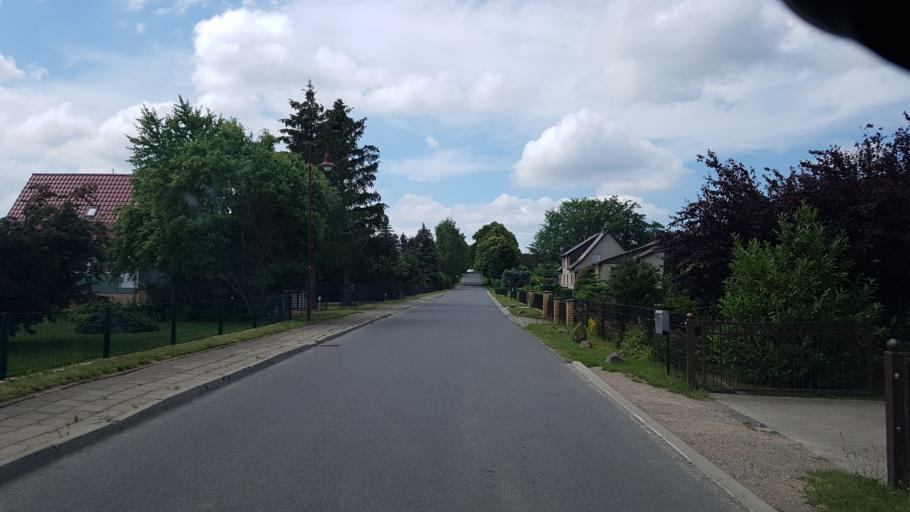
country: DE
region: Mecklenburg-Vorpommern
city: Strasburg
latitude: 53.4317
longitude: 13.7025
